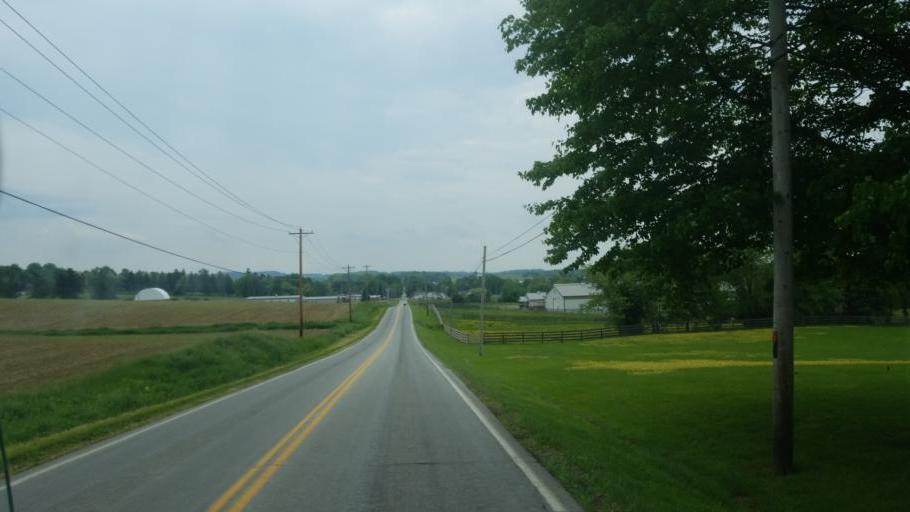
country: US
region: Ohio
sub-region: Wayne County
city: Apple Creek
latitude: 40.7617
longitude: -81.8438
